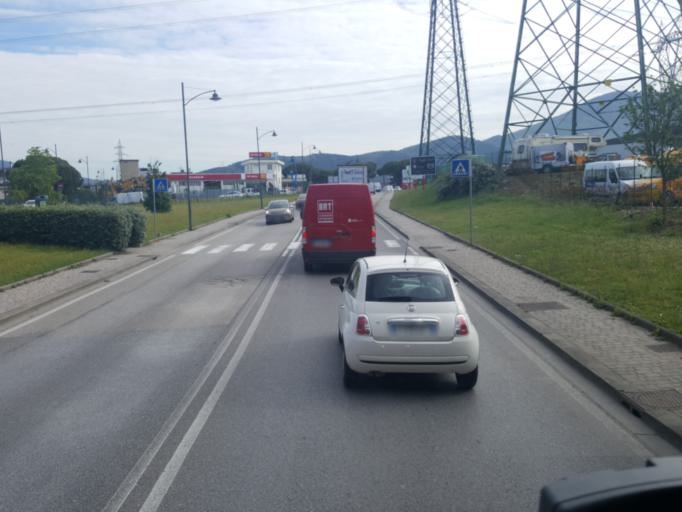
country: IT
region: Tuscany
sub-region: Province of Florence
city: Calenzano
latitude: 43.8490
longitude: 11.1627
